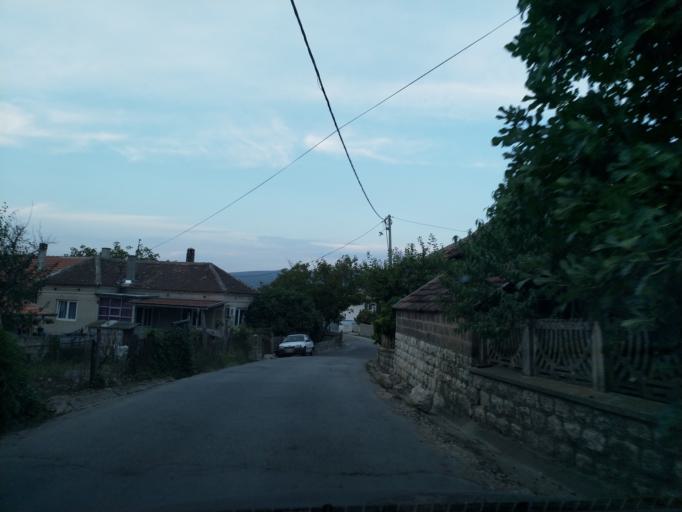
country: RS
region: Central Serbia
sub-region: Pomoravski Okrug
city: Paracin
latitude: 43.8508
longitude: 21.5281
